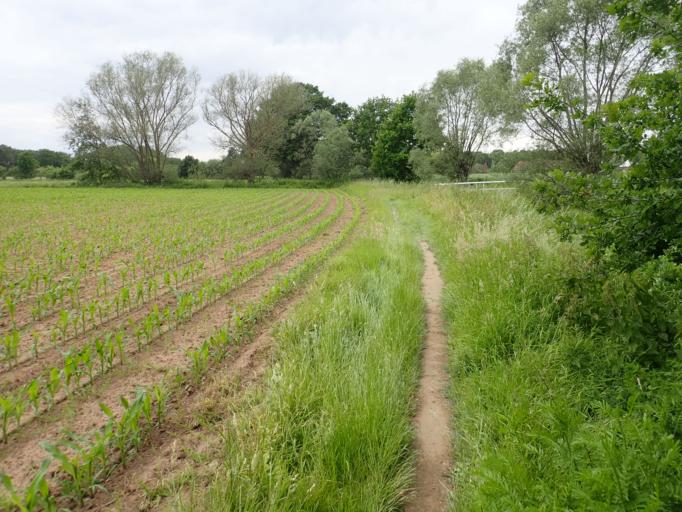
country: BE
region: Flanders
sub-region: Provincie Vlaams-Brabant
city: Haacht
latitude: 50.9788
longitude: 4.6518
